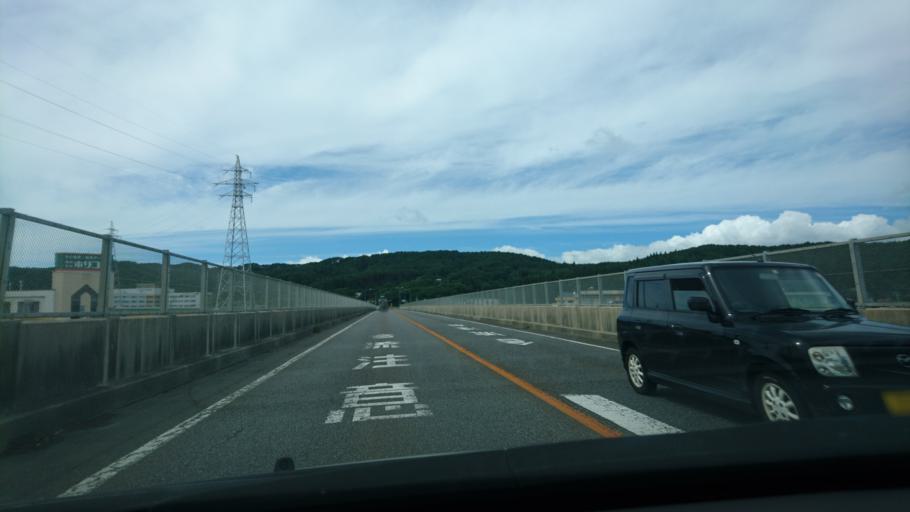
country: JP
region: Aomori
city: Hachinohe
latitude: 40.1967
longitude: 141.7826
